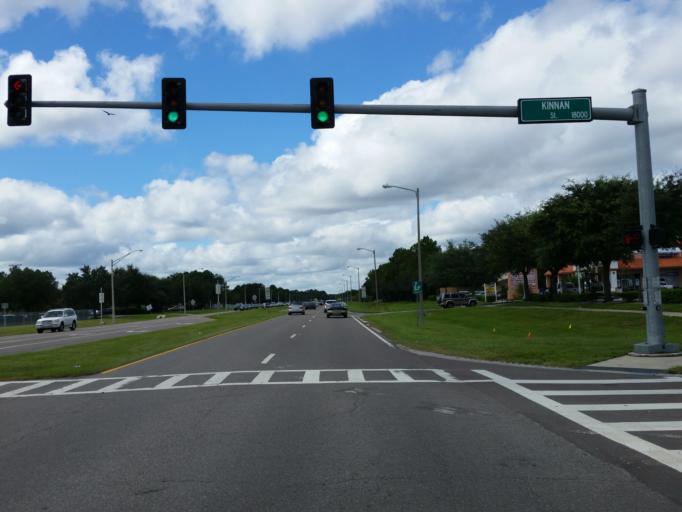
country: US
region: Florida
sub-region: Hillsborough County
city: Pebble Creek
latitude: 28.1422
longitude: -82.3259
